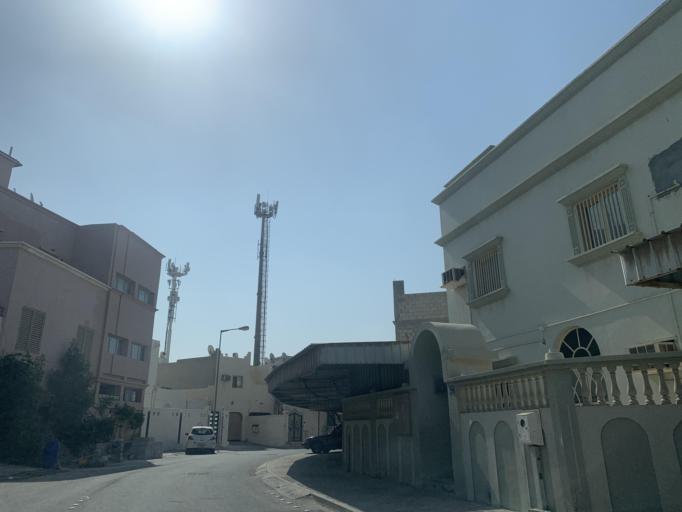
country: BH
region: Central Governorate
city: Madinat Hamad
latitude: 26.1257
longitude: 50.5044
